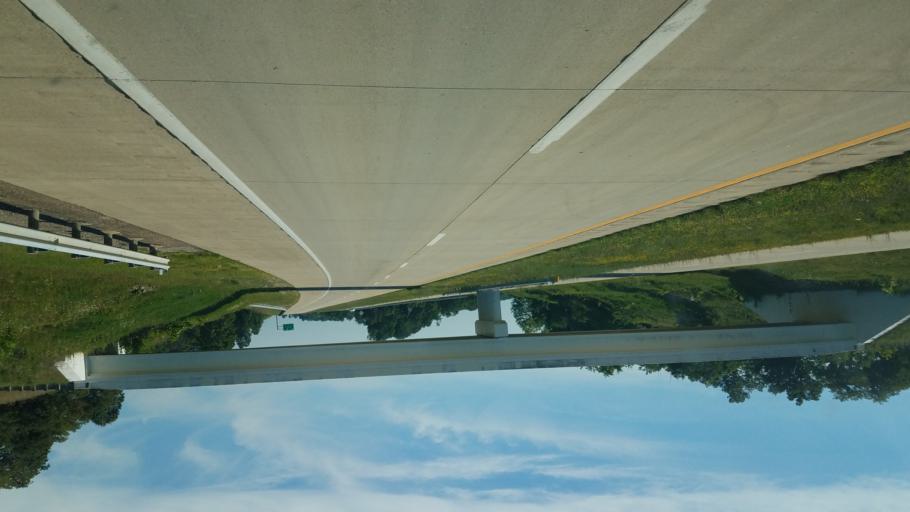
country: US
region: Ohio
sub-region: Athens County
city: Athens
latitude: 39.2778
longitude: -82.0985
